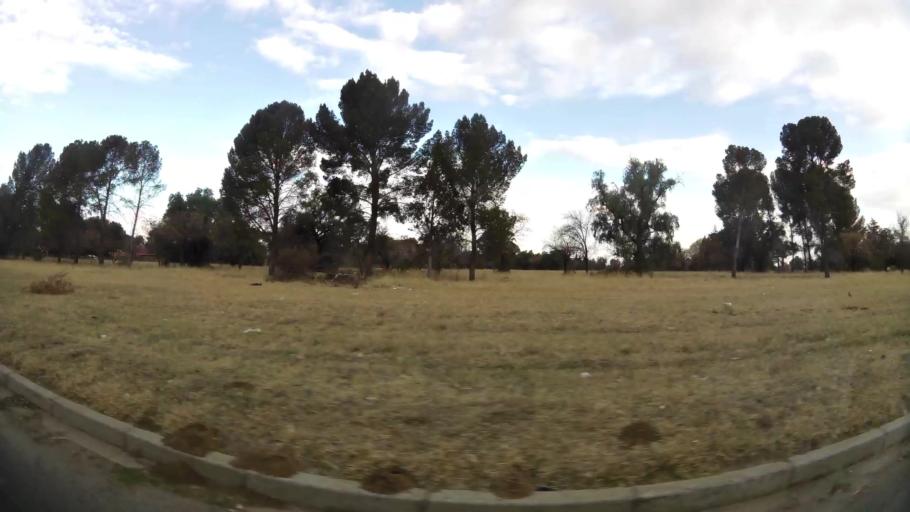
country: ZA
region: Orange Free State
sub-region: Lejweleputswa District Municipality
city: Welkom
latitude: -27.9956
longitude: 26.7163
